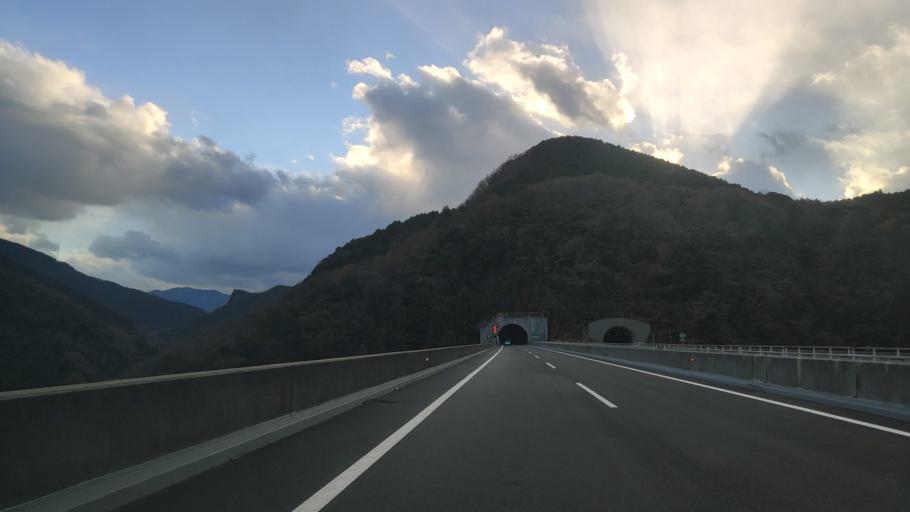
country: JP
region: Ehime
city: Saijo
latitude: 33.8462
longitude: 132.9941
